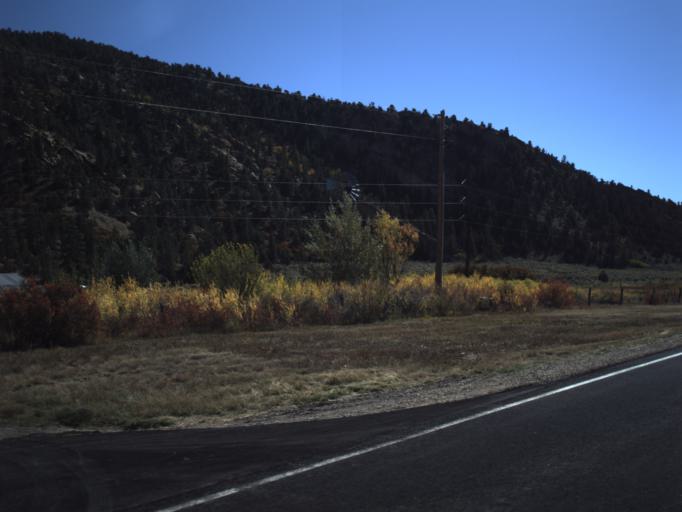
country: US
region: Utah
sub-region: Garfield County
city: Panguitch
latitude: 37.7195
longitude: -111.7815
